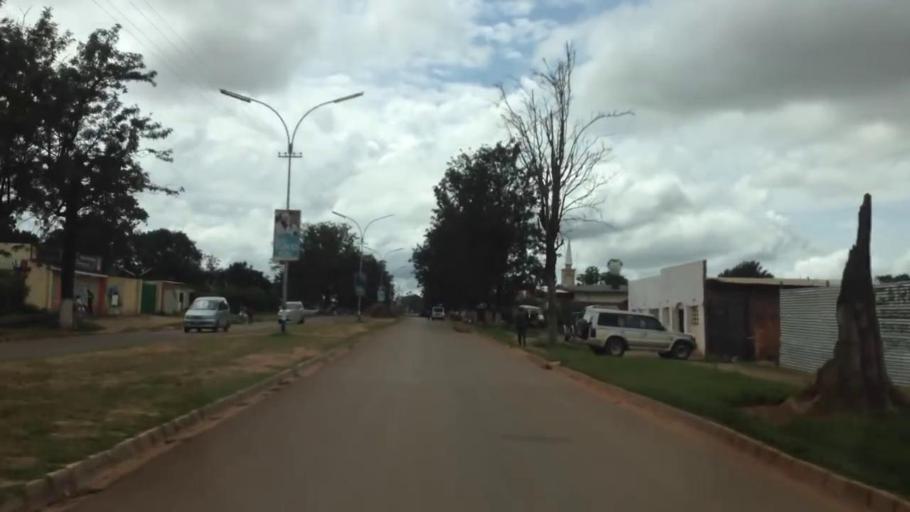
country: CD
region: Katanga
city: Kolwezi
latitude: -10.7190
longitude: 25.5005
